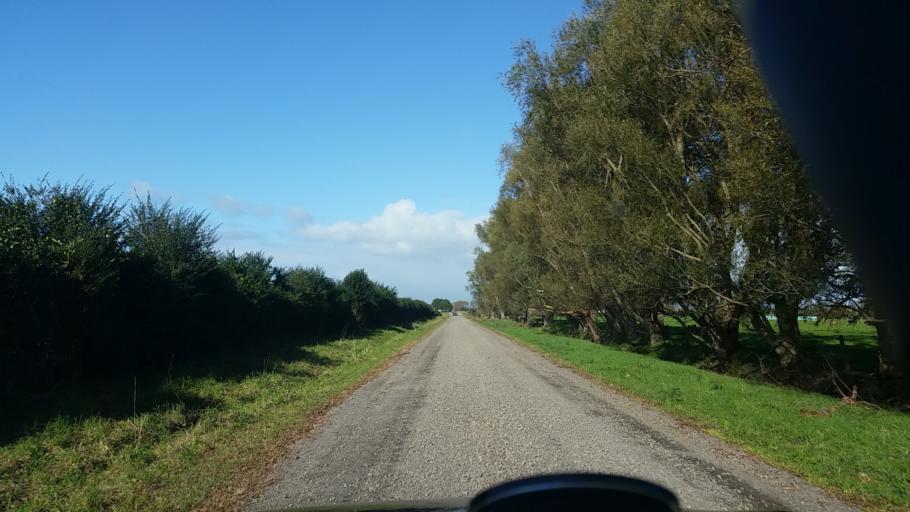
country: NZ
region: Bay of Plenty
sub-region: Western Bay of Plenty District
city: Katikati
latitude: -37.5883
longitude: 175.7132
